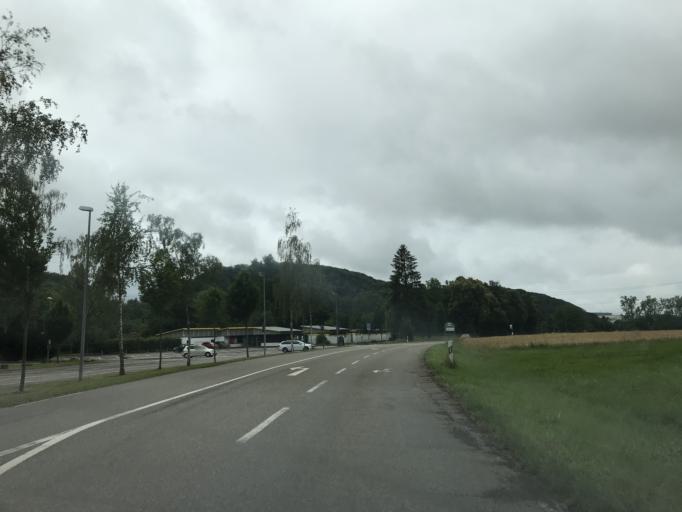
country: DE
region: Baden-Wuerttemberg
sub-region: Freiburg Region
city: Steinen
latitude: 47.6423
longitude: 7.7262
